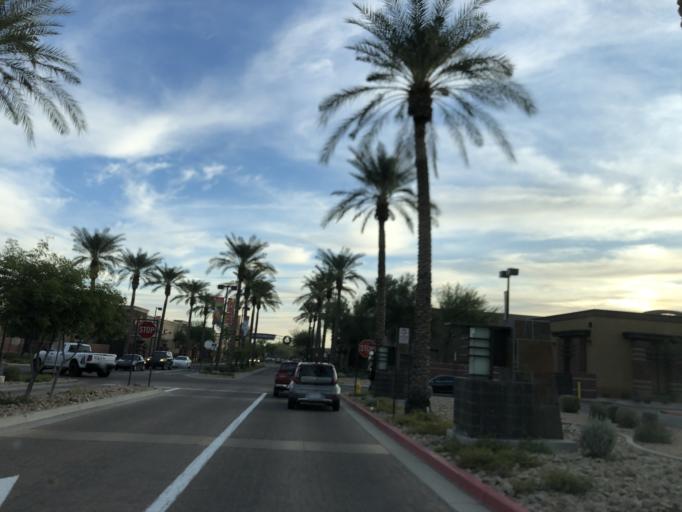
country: US
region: Arizona
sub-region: Maricopa County
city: Anthem
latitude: 33.7122
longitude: -112.1118
